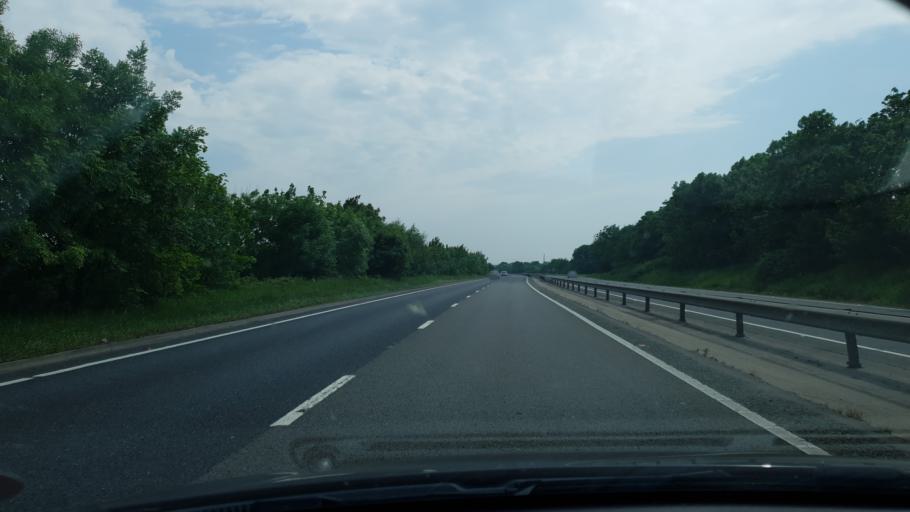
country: GB
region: England
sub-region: Bedford
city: Pertenhall
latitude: 52.3422
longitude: -0.3391
